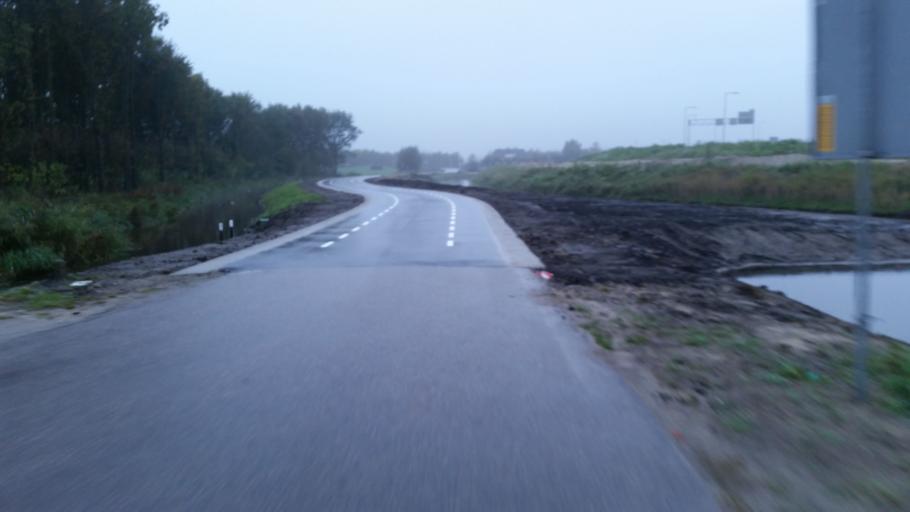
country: NL
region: North Holland
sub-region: Gemeente Ouder-Amstel
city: Ouderkerk aan de Amstel
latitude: 52.2953
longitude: 4.9364
